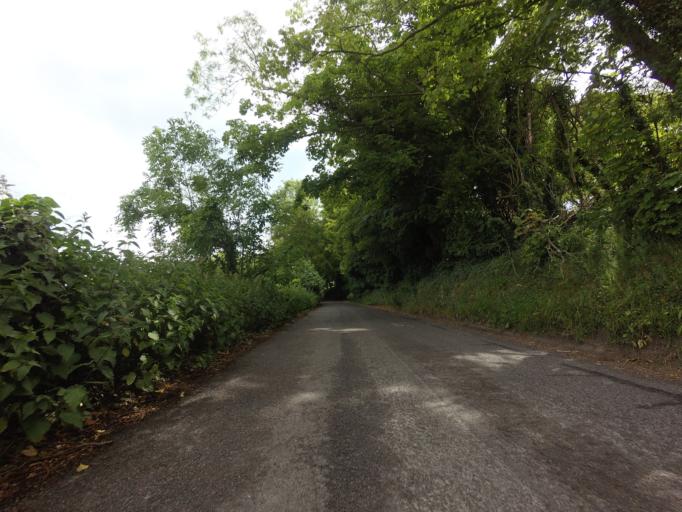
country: GB
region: England
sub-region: Kent
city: Shoreham
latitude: 51.3393
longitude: 0.1713
